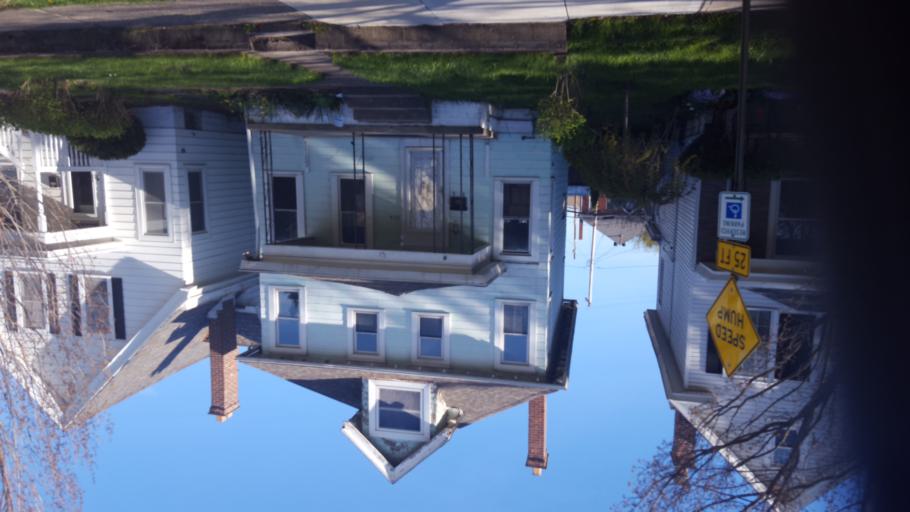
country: US
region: Ohio
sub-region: Franklin County
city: Columbus
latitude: 39.9366
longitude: -82.9897
